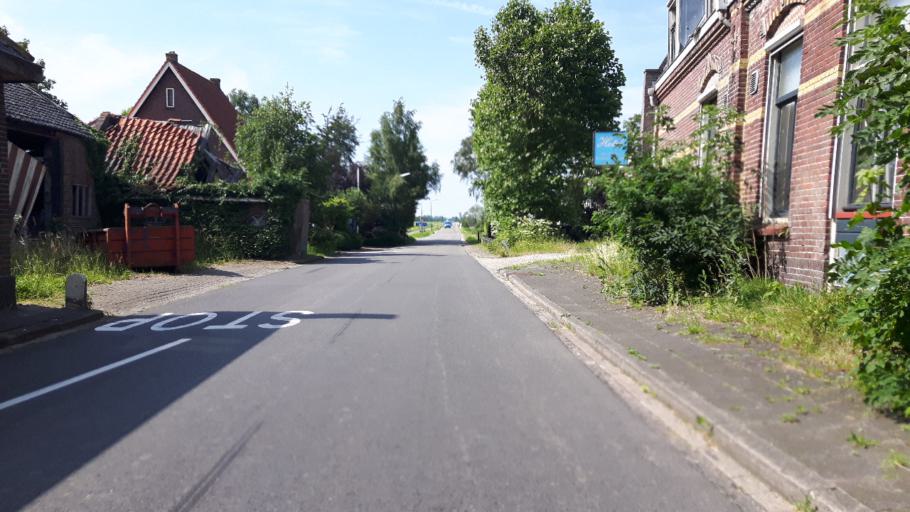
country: NL
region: Utrecht
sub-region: Gemeente Oudewater
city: Oudewater
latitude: 51.9957
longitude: 4.9030
